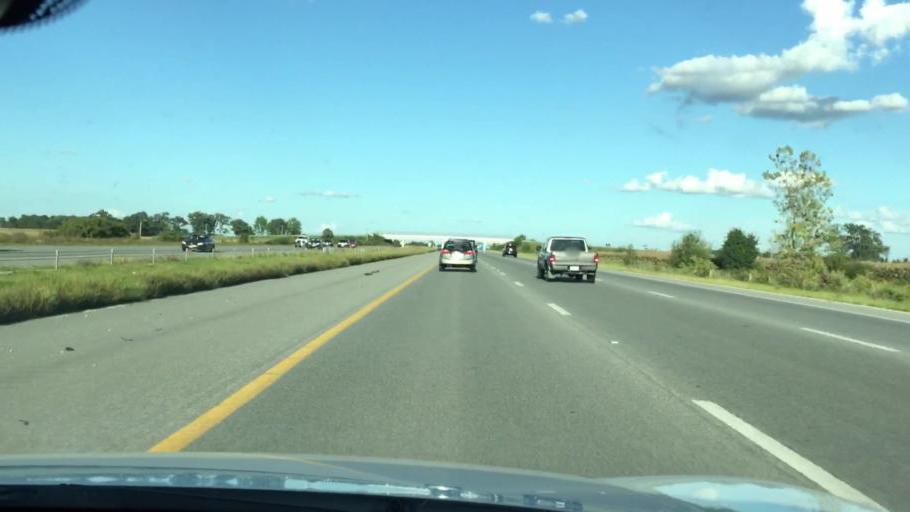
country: US
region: Ohio
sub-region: Madison County
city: London
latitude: 39.9506
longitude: -83.4093
